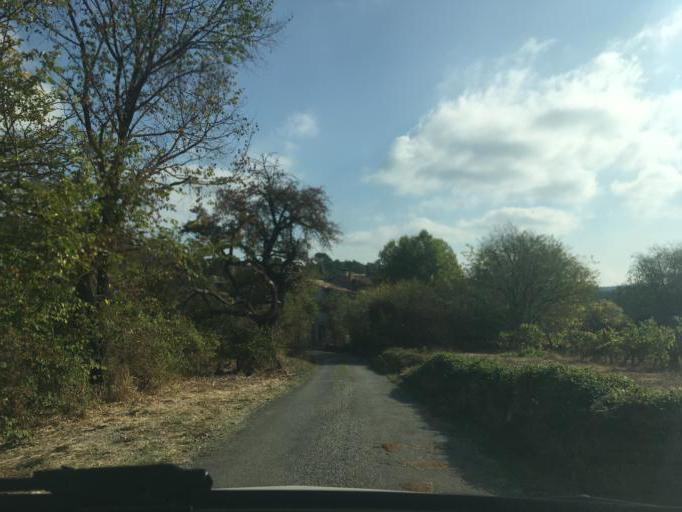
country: FR
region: Provence-Alpes-Cote d'Azur
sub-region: Departement du Var
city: Lorgues
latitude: 43.4855
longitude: 6.3996
